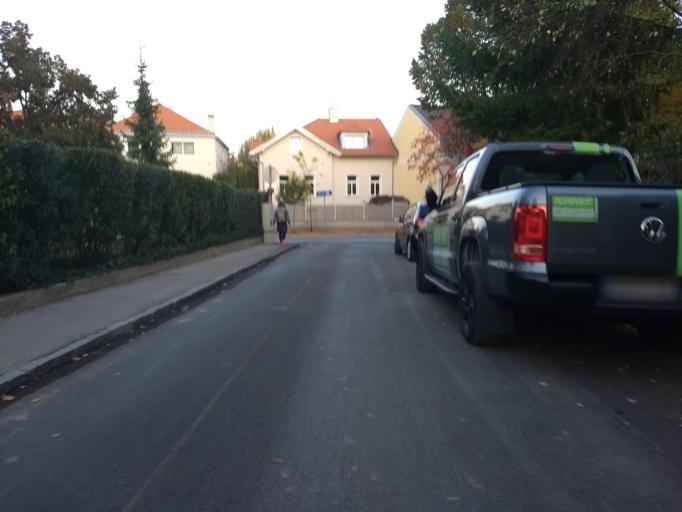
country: AT
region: Lower Austria
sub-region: Politischer Bezirk Modling
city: Perchtoldsdorf
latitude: 48.1245
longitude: 16.2578
